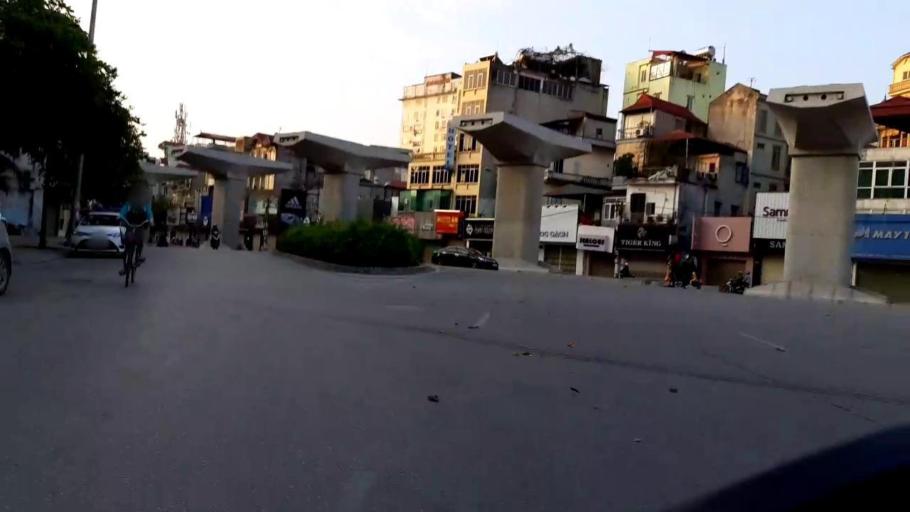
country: VN
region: Ha Noi
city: Cau Giay
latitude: 21.0341
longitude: 105.7976
